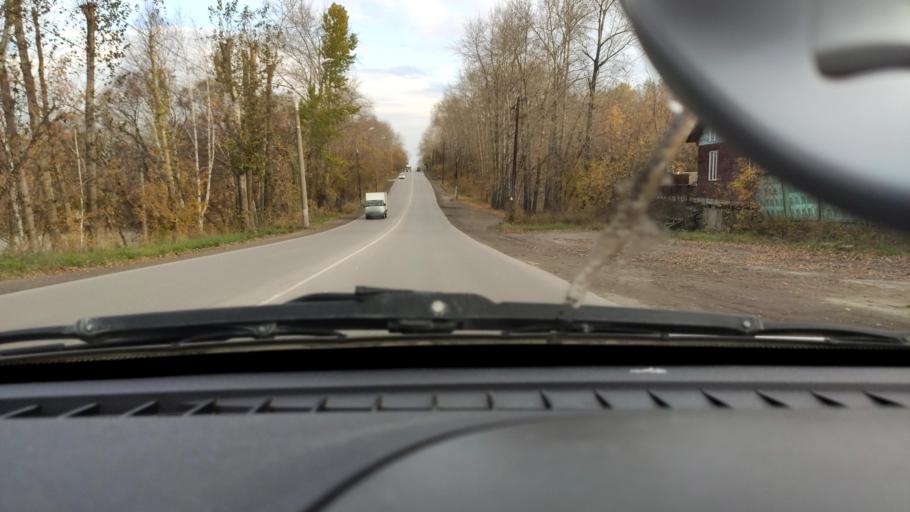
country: RU
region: Perm
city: Perm
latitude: 58.1235
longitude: 56.3704
